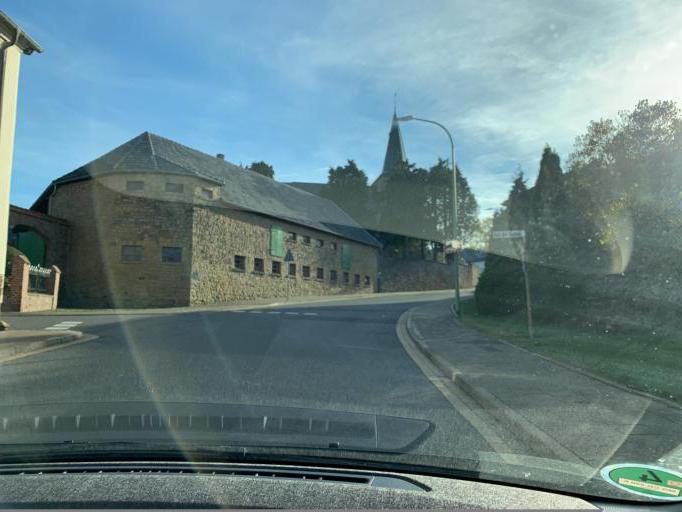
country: DE
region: North Rhine-Westphalia
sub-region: Regierungsbezirk Koln
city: Nideggen
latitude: 50.6784
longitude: 6.5192
